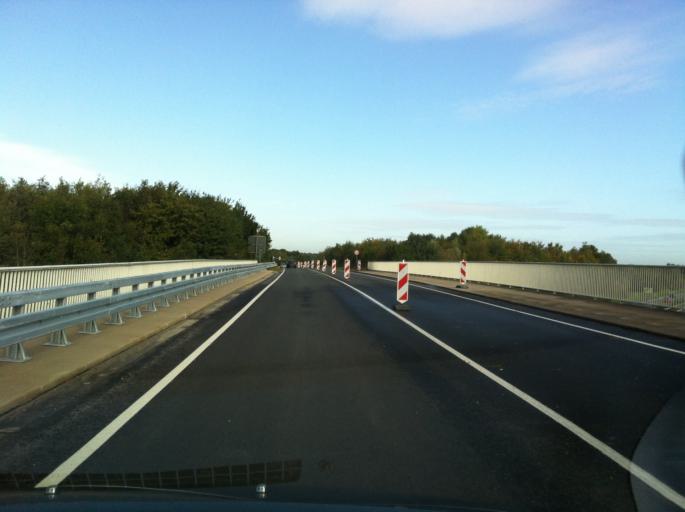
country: DE
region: North Rhine-Westphalia
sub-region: Regierungsbezirk Munster
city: Ochtrup
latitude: 52.2489
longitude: 7.1657
